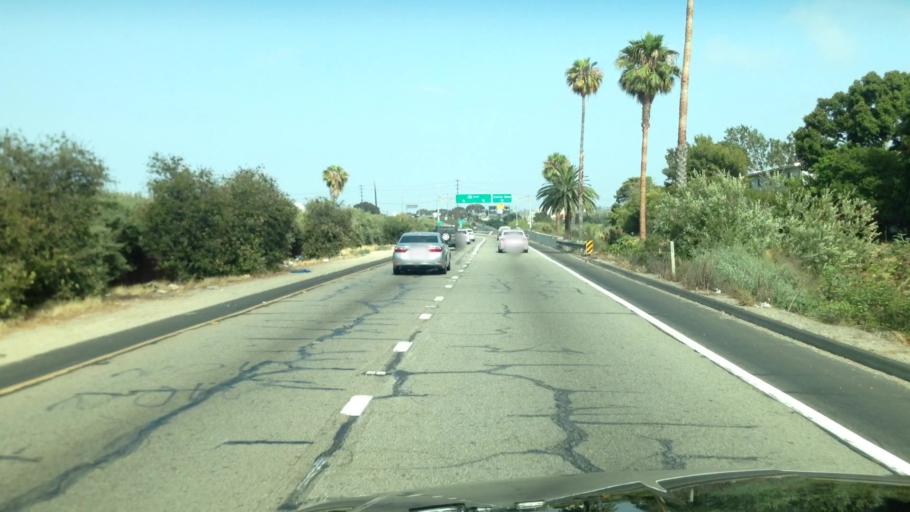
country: US
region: California
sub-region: Los Angeles County
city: Marina del Rey
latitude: 33.9822
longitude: -118.4341
